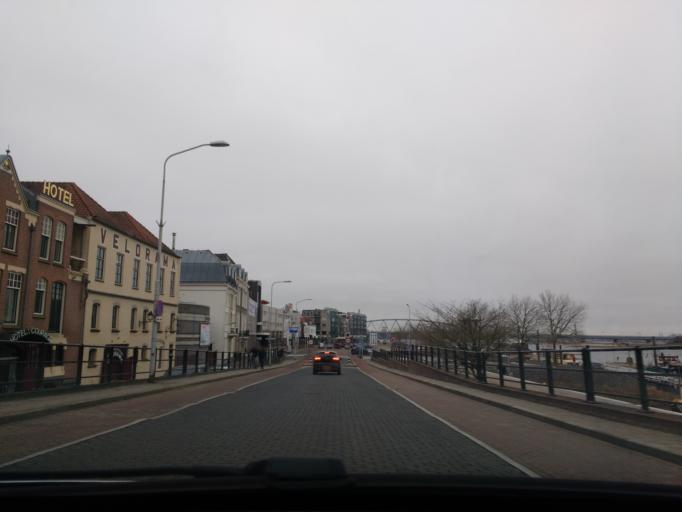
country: NL
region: Gelderland
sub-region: Gemeente Nijmegen
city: Nijmegen
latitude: 51.8487
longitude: 5.8707
